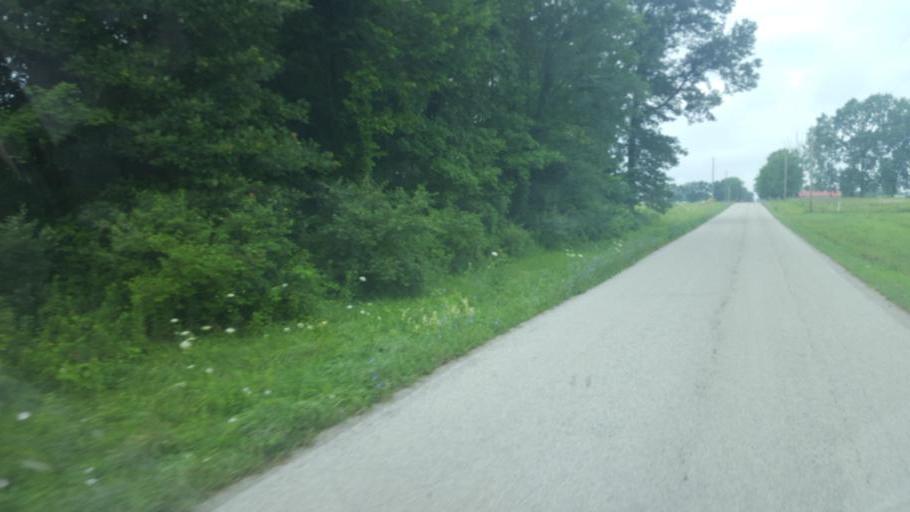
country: US
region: Ohio
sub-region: Knox County
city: Centerburg
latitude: 40.3809
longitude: -82.7662
